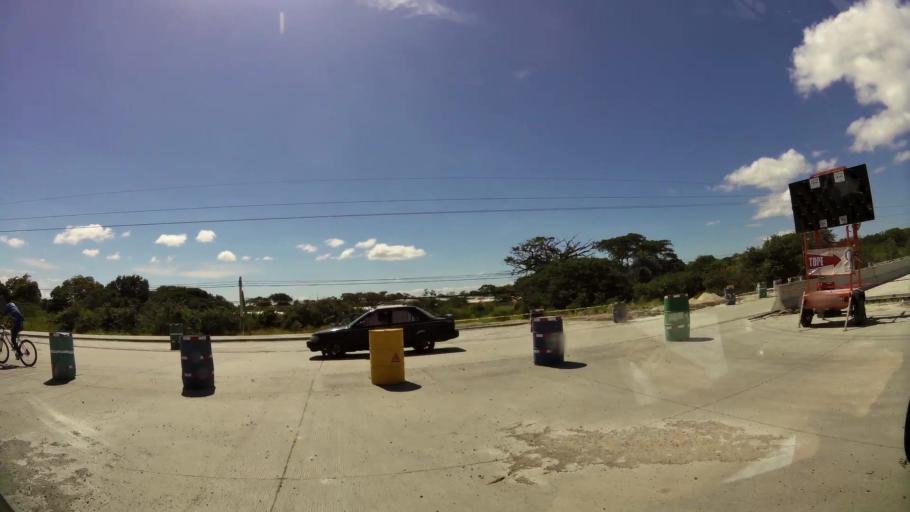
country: CR
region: Guanacaste
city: Bagaces
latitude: 10.5205
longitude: -85.2523
